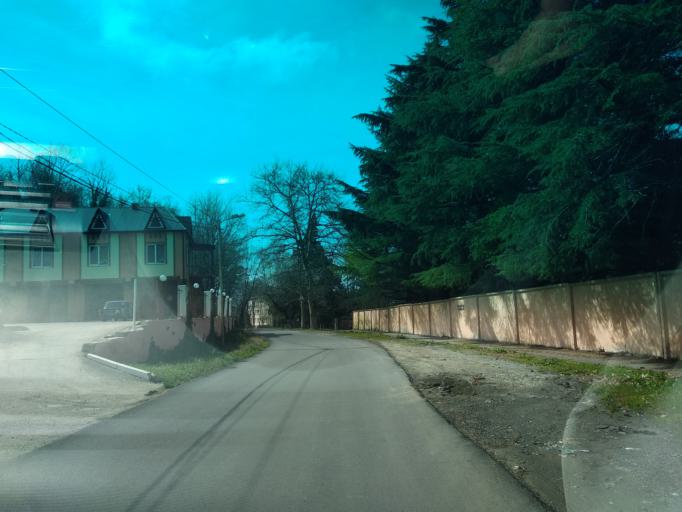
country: RU
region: Krasnodarskiy
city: Shepsi
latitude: 44.0368
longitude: 39.1503
